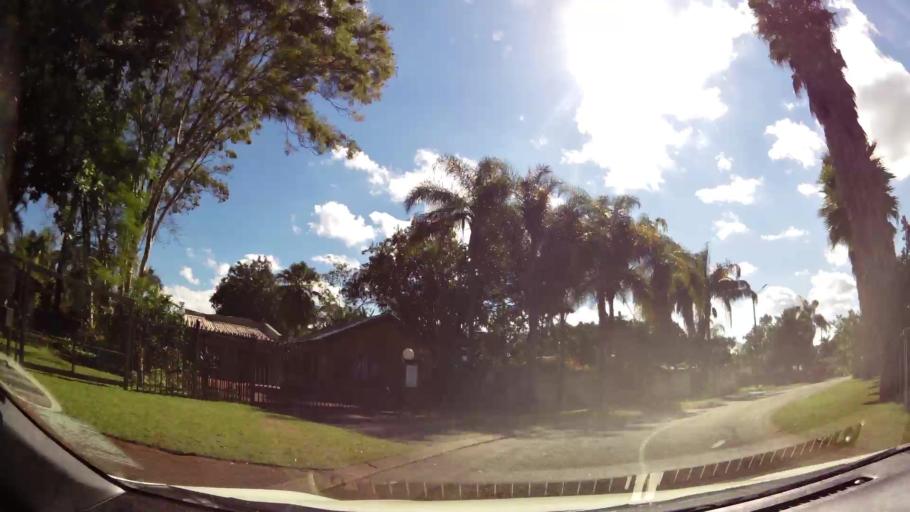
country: ZA
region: Limpopo
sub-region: Mopani District Municipality
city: Tzaneen
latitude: -23.8172
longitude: 30.1471
